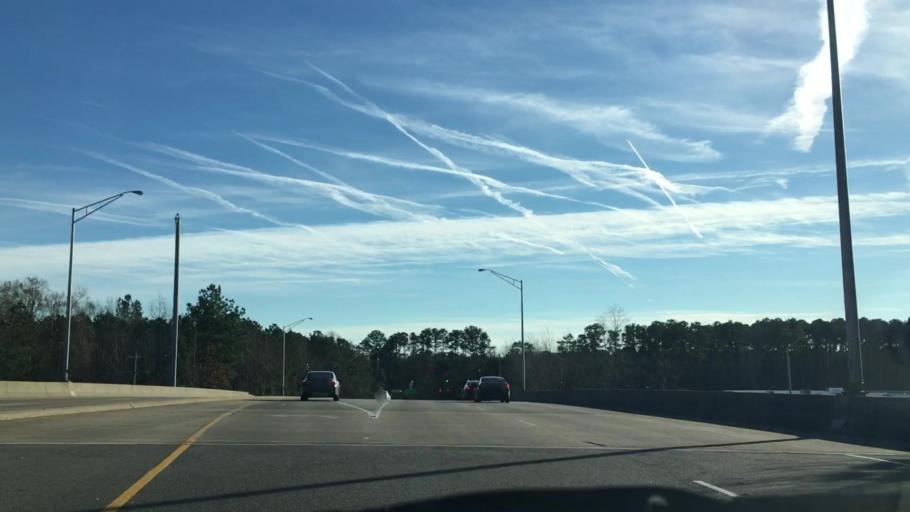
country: US
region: Virginia
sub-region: City of Portsmouth
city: Portsmouth Heights
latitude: 36.8679
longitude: -76.4224
